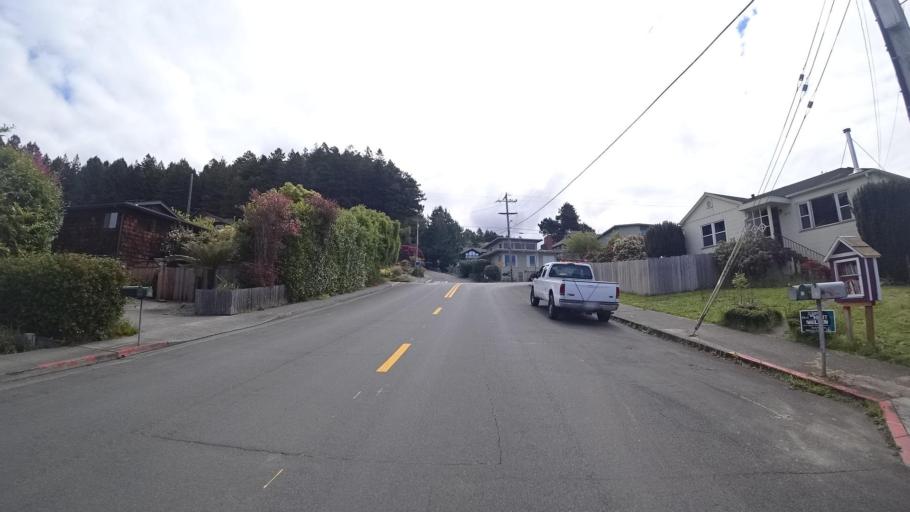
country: US
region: California
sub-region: Humboldt County
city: Arcata
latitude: 40.8685
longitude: -124.0763
